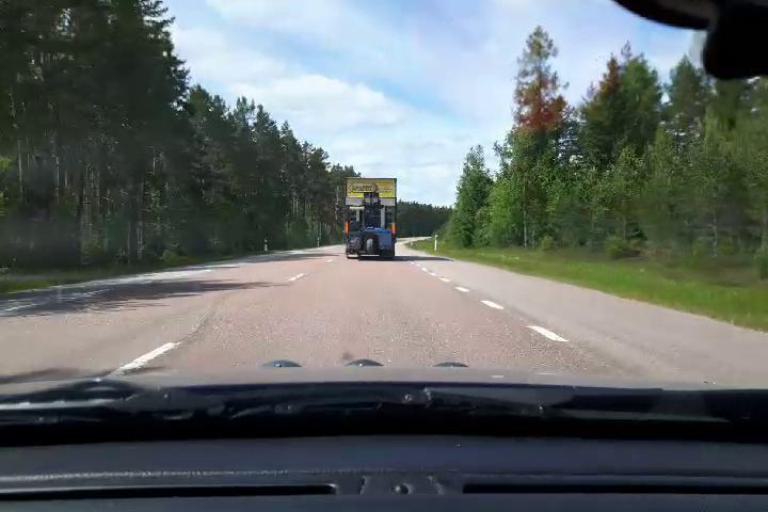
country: SE
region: Uppsala
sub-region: Osthammars Kommun
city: Bjorklinge
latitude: 60.1118
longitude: 17.5285
